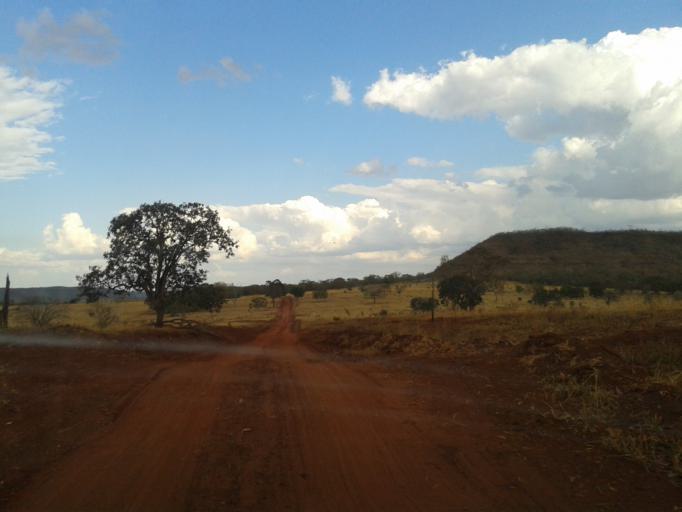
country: BR
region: Minas Gerais
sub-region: Santa Vitoria
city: Santa Vitoria
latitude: -19.1934
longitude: -49.9417
